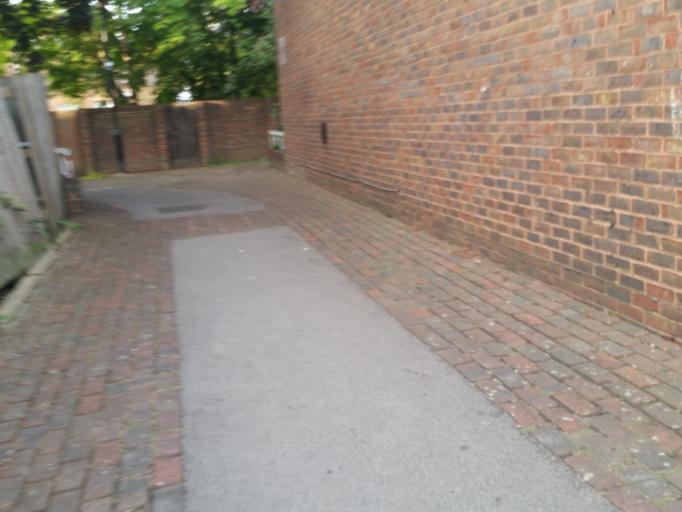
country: GB
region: England
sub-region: Greater London
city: Wood Green
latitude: 51.5951
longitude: -0.1118
